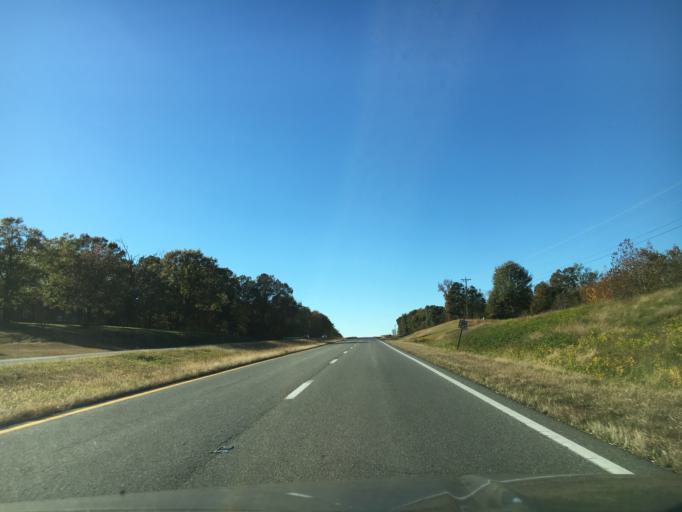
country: US
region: Virginia
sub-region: Halifax County
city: South Boston
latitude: 36.6828
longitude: -78.8471
